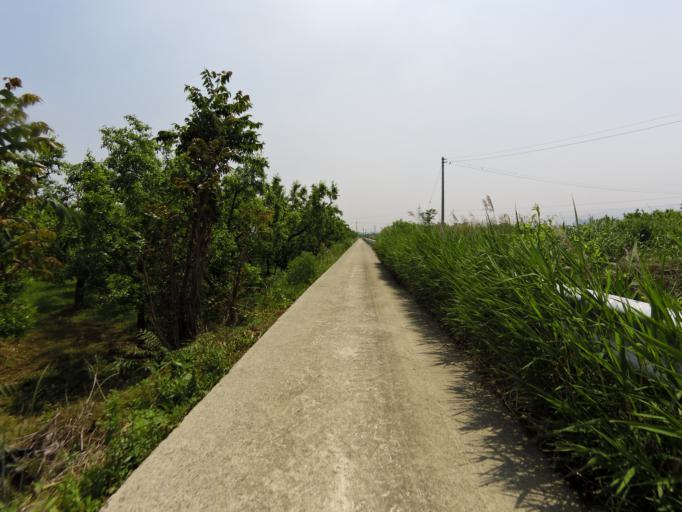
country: KR
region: Gyeongsangbuk-do
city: Gyeongsan-si
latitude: 35.8494
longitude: 128.7308
